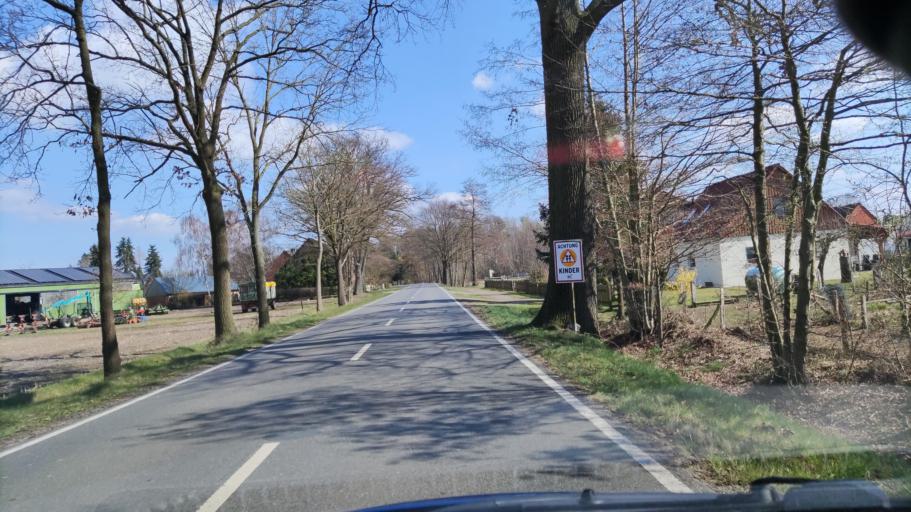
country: DE
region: Lower Saxony
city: Woltersdorf
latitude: 53.0038
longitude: 11.2491
